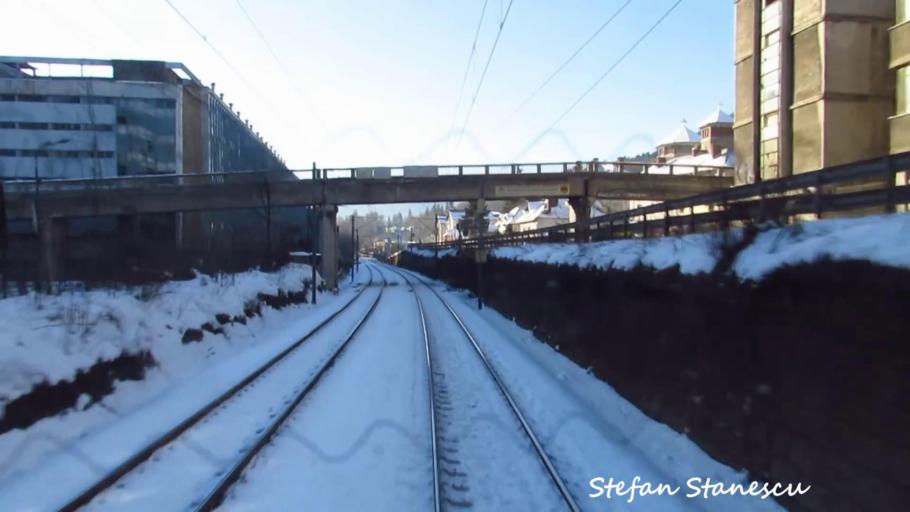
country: RO
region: Prahova
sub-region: Oras Sinaia
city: Sinaia
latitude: 45.3421
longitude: 25.5511
